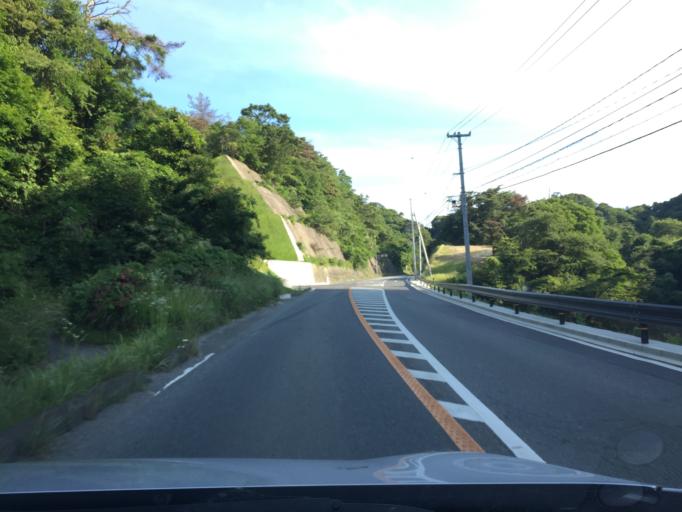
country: JP
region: Fukushima
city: Iwaki
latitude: 37.0018
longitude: 140.9674
